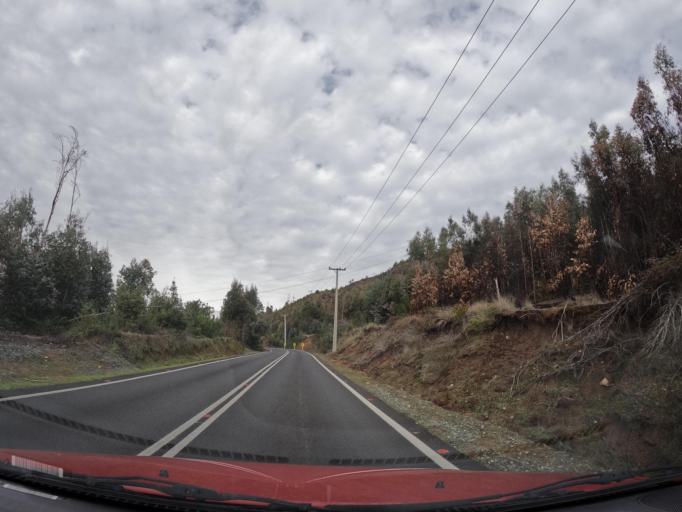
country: CL
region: Maule
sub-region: Provincia de Linares
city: Linares
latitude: -35.9234
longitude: -71.4486
